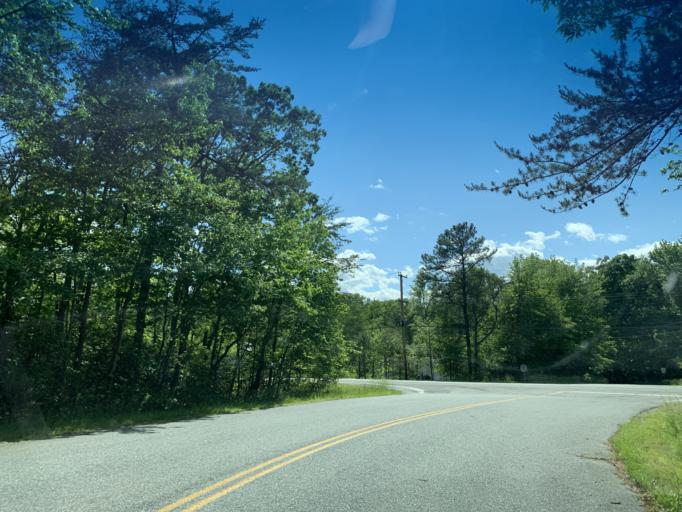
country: US
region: Maryland
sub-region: Cecil County
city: Charlestown
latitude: 39.5436
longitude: -75.9480
